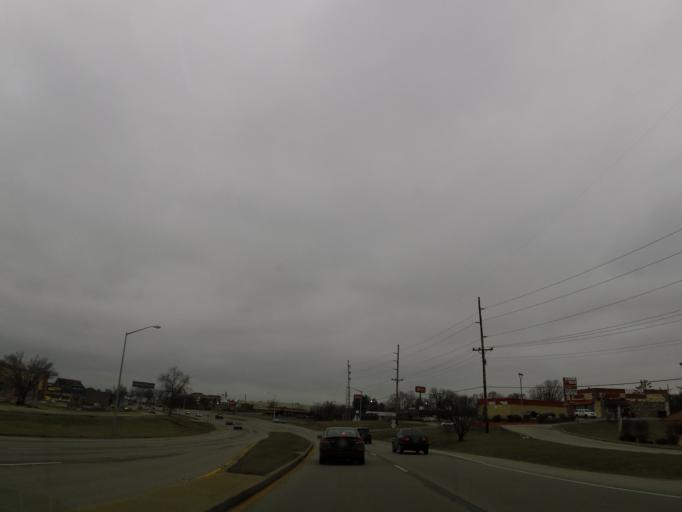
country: US
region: Kentucky
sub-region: Franklin County
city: Frankfort
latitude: 38.1711
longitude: -84.8995
